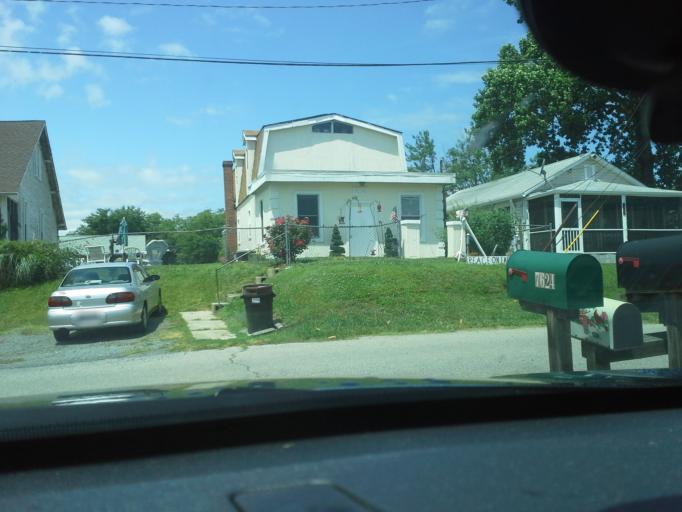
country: US
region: Maryland
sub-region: Calvert County
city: Chesapeake Beach
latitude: 38.6858
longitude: -76.5347
